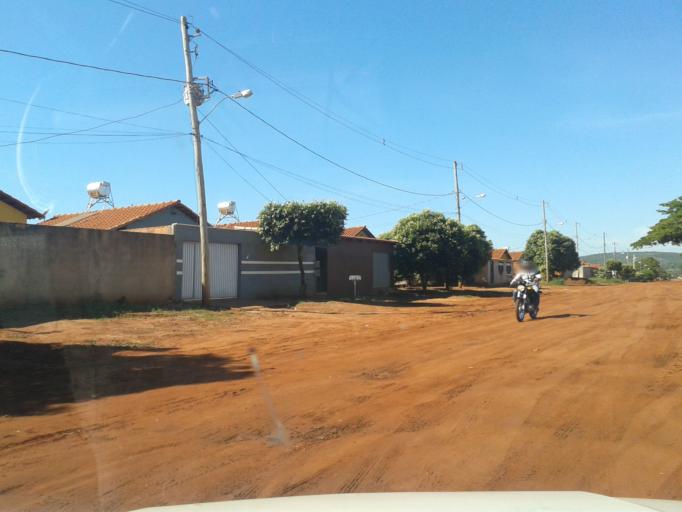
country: BR
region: Minas Gerais
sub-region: Ituiutaba
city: Ituiutaba
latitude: -19.2042
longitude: -49.7844
